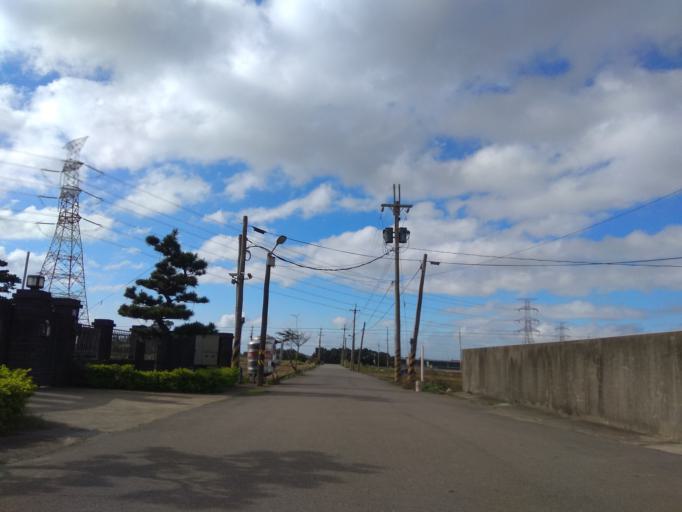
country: TW
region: Taiwan
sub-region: Hsinchu
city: Zhubei
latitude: 24.9723
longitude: 121.0769
